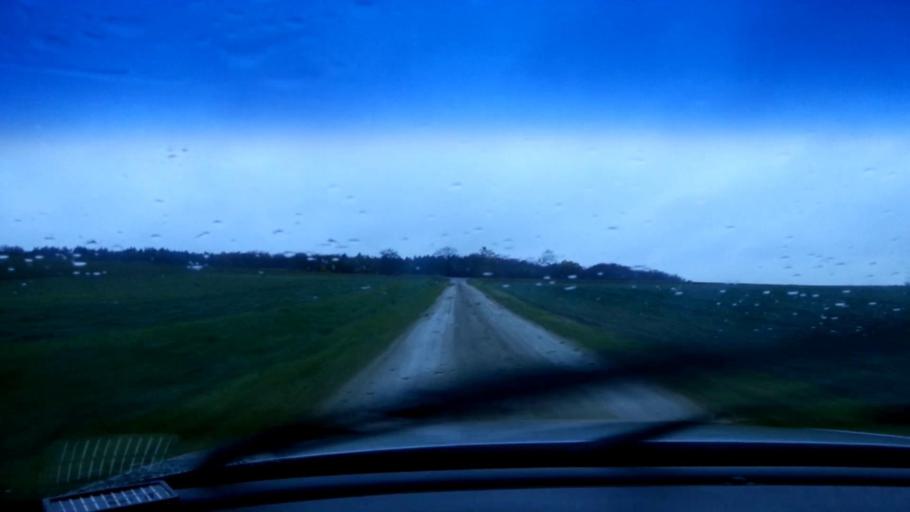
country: DE
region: Bavaria
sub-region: Upper Franconia
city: Memmelsdorf
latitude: 49.9529
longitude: 10.9505
